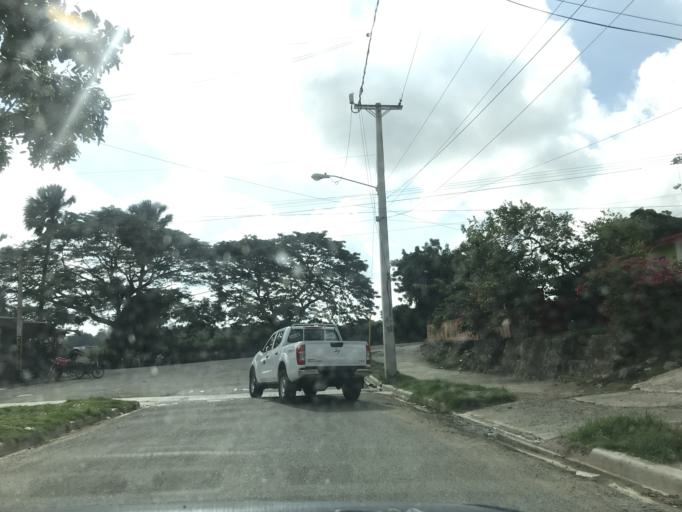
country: DO
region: Santiago
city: Santiago de los Caballeros
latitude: 19.4492
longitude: -70.7306
